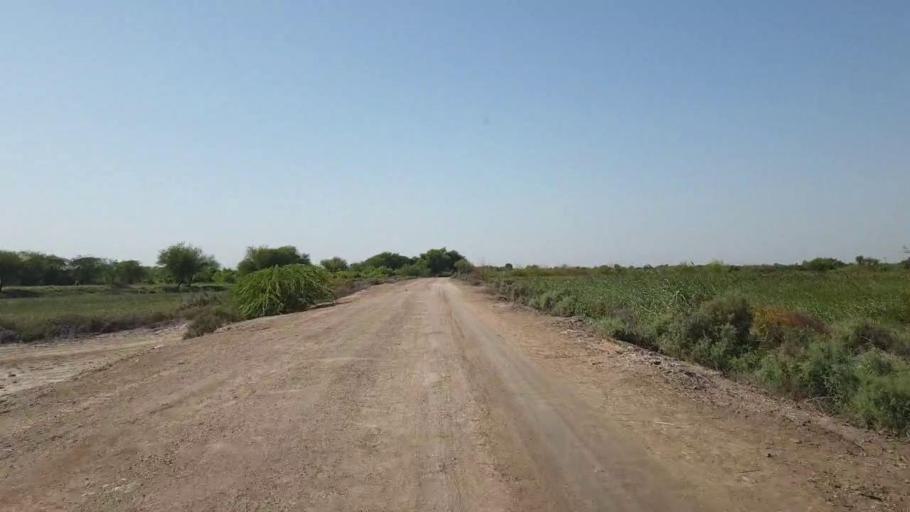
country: PK
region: Sindh
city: Tando Bago
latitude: 24.7048
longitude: 69.0332
